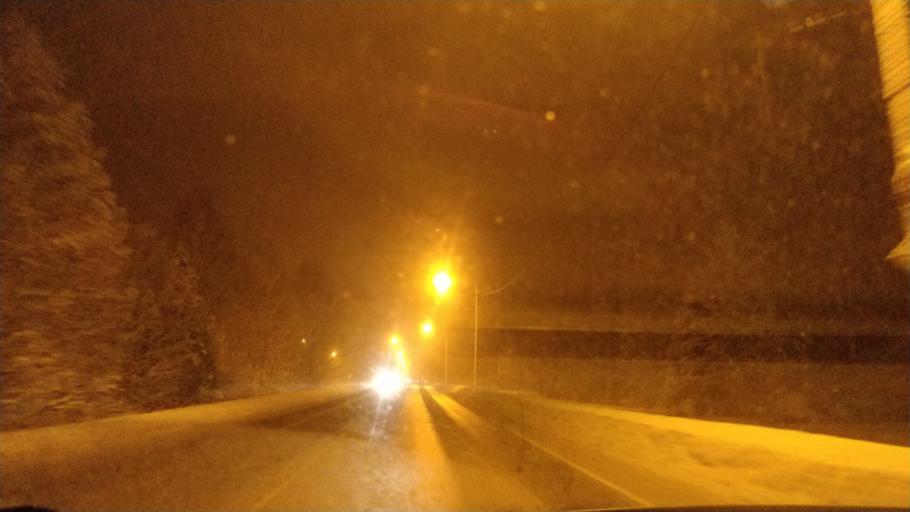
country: FI
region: Lapland
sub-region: Rovaniemi
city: Rovaniemi
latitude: 66.4776
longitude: 25.6239
